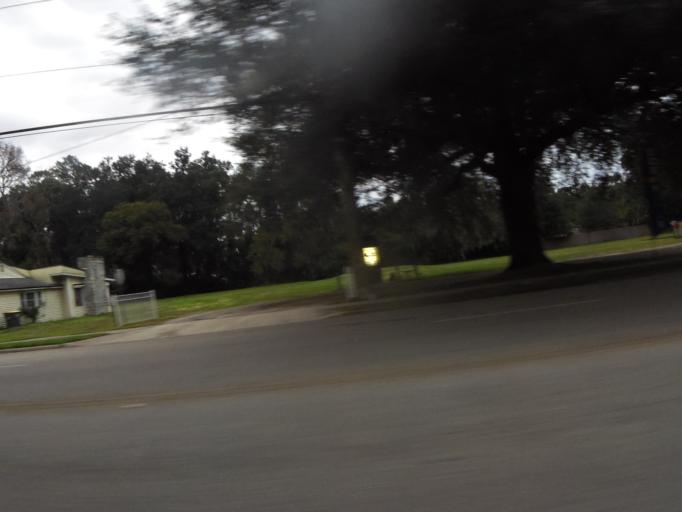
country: US
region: Florida
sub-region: Duval County
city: Jacksonville
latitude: 30.2643
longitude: -81.5932
